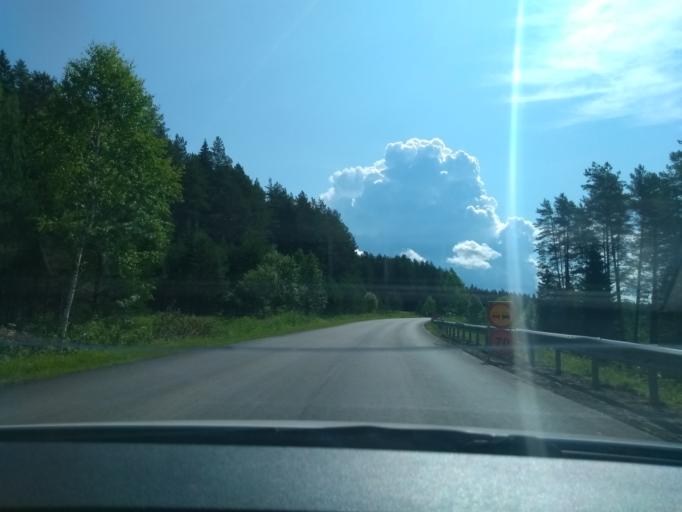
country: RU
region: Perm
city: Bershet'
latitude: 57.8212
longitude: 56.5203
